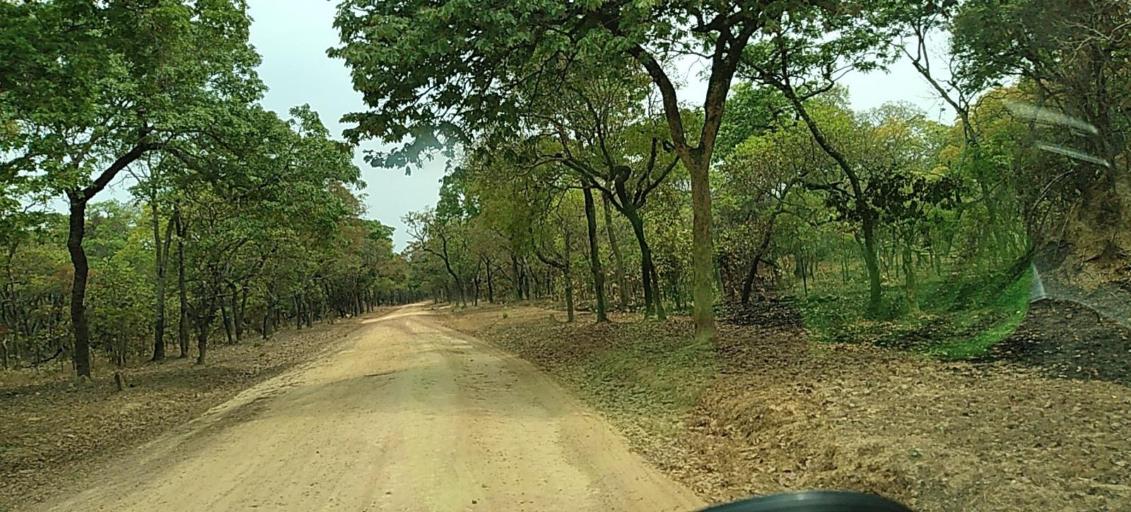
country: ZM
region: North-Western
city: Solwezi
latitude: -12.9340
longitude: 26.5594
